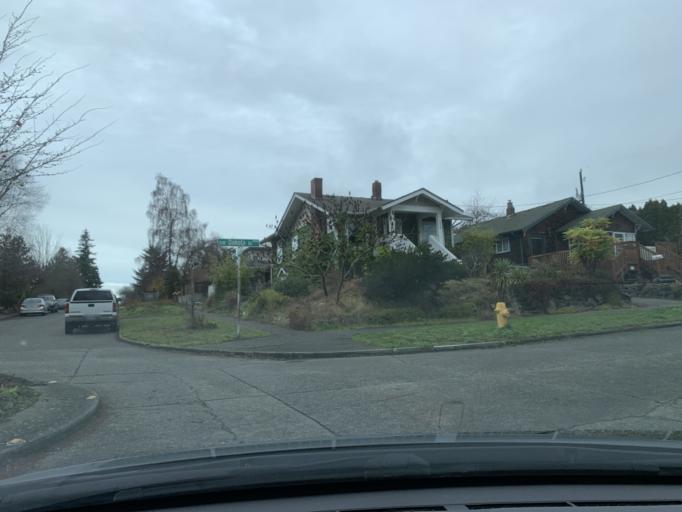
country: US
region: Washington
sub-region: King County
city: White Center
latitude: 47.5666
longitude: -122.3921
